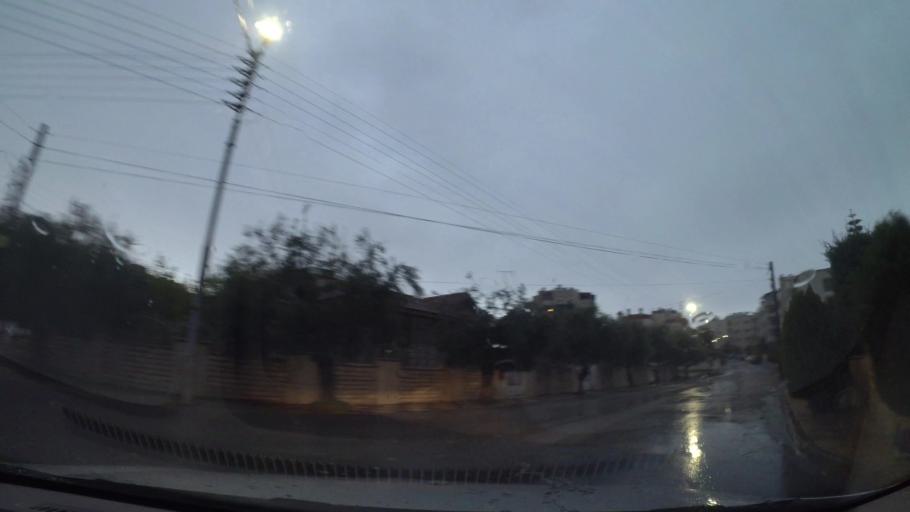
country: JO
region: Amman
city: Umm as Summaq
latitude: 31.9026
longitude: 35.8608
